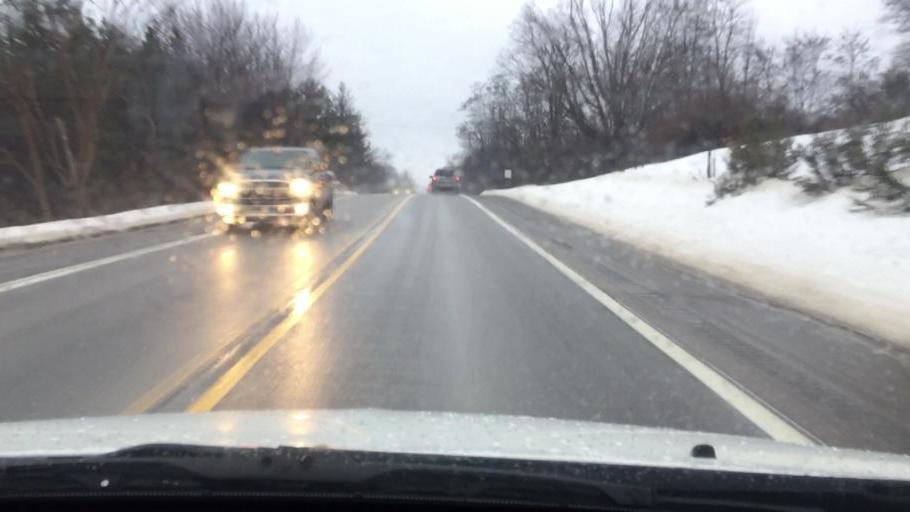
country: US
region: Michigan
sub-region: Charlevoix County
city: East Jordan
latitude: 45.2441
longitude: -85.1810
